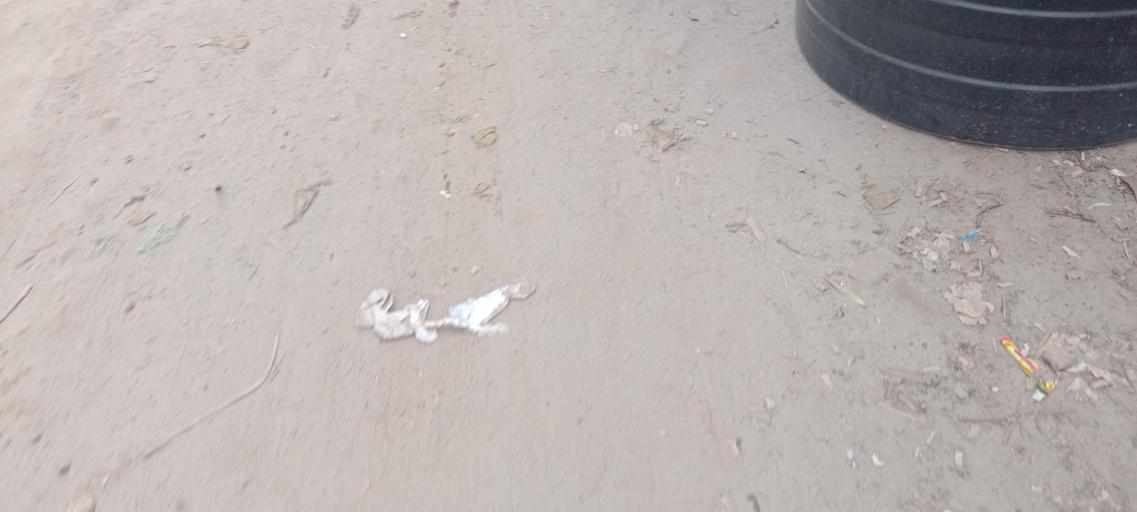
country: BD
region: Dhaka
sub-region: Dhaka
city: Dhaka
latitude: 23.6662
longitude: 90.4203
